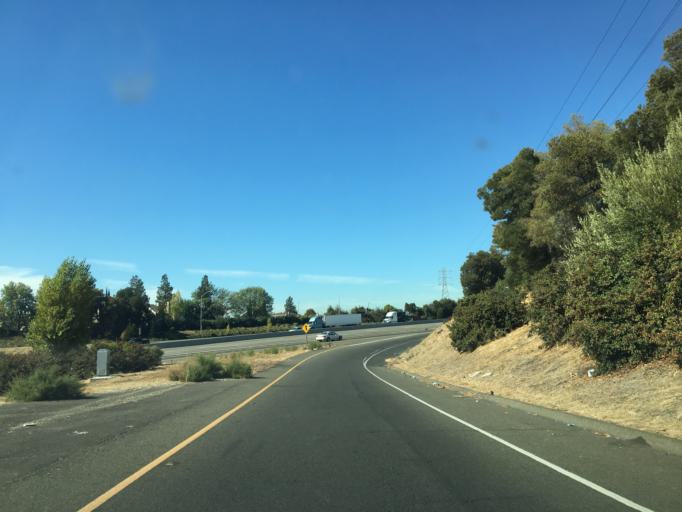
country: US
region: California
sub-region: Santa Clara County
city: Alum Rock
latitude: 37.3693
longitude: -121.8460
